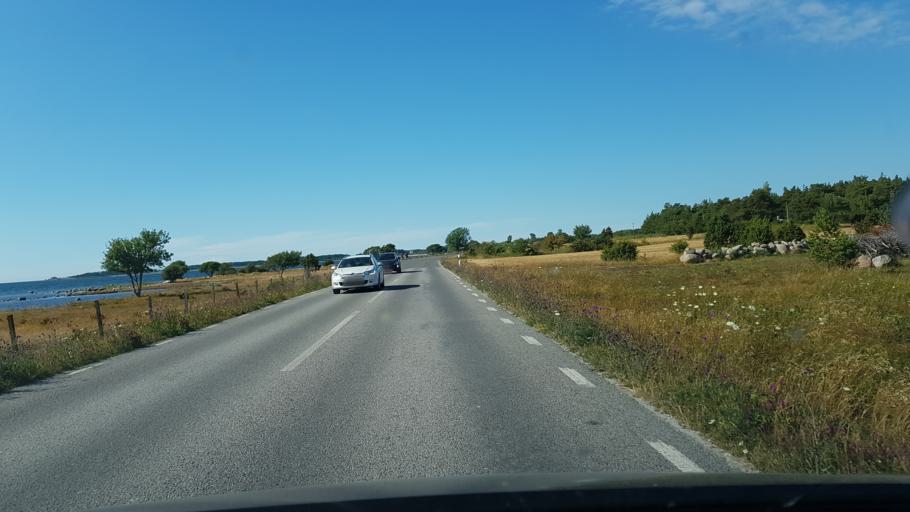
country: SE
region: Gotland
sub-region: Gotland
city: Klintehamn
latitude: 57.4212
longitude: 18.1498
